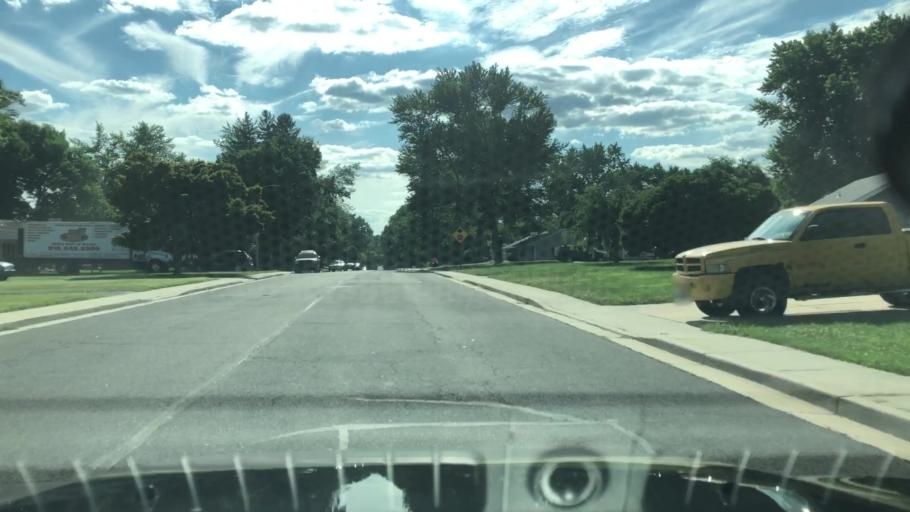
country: US
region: Pennsylvania
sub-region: Bucks County
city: Fairless Hills
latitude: 40.1837
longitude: -74.8420
